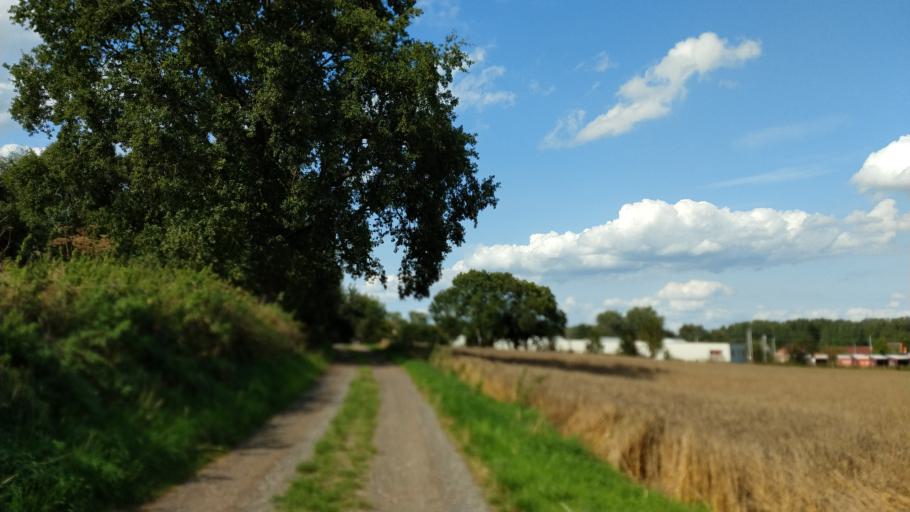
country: BE
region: Flanders
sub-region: Provincie Vlaams-Brabant
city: Boutersem
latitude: 50.8331
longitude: 4.8474
